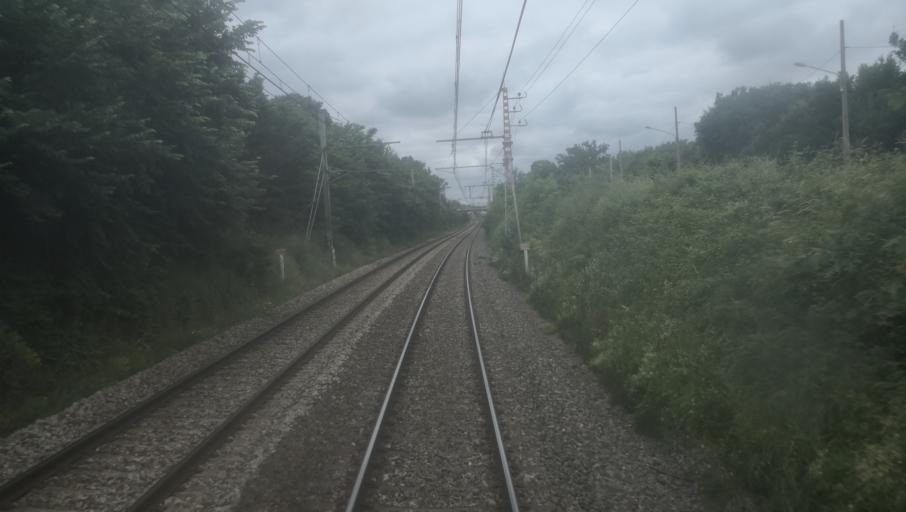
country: FR
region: Midi-Pyrenees
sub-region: Departement de la Haute-Garonne
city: Saint-Orens-de-Gameville
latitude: 43.5571
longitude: 1.5039
